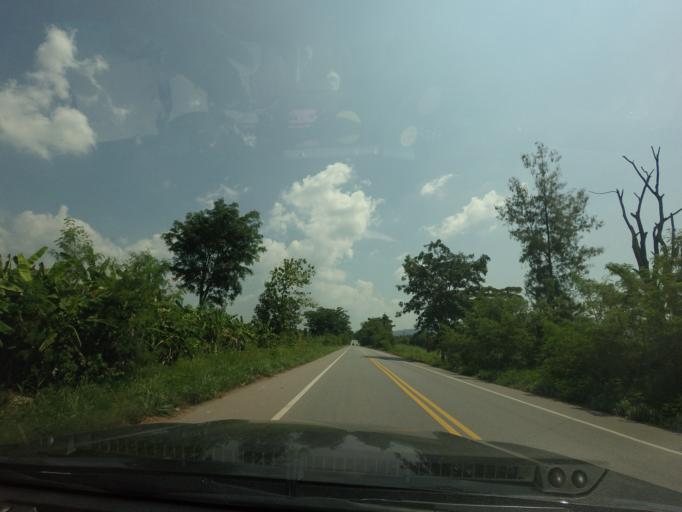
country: TH
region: Uttaradit
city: Thong Saen Khan
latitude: 17.3018
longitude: 100.4033
